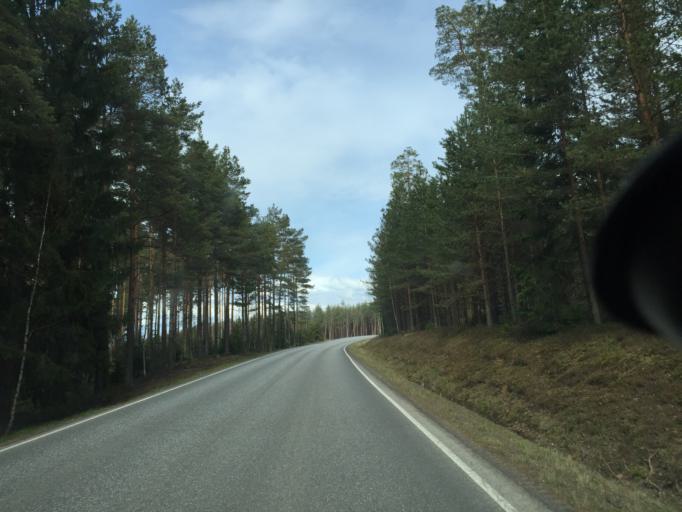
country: FI
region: Varsinais-Suomi
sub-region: Salo
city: Pernioe
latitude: 60.0187
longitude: 23.1685
